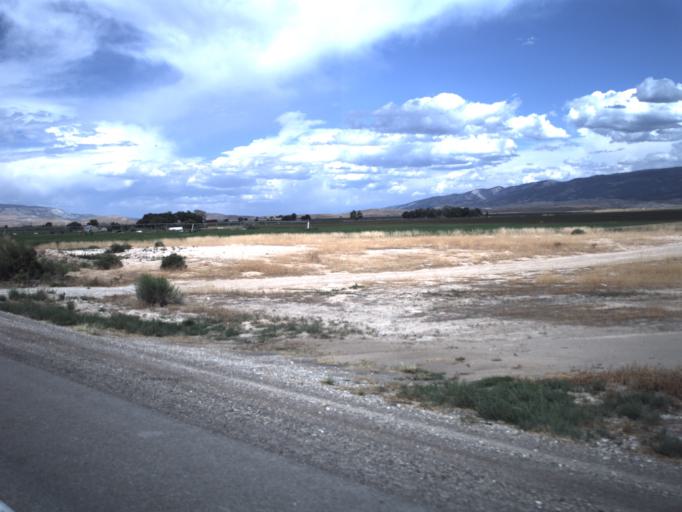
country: US
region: Utah
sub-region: Sanpete County
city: Centerfield
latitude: 39.0644
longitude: -111.8208
